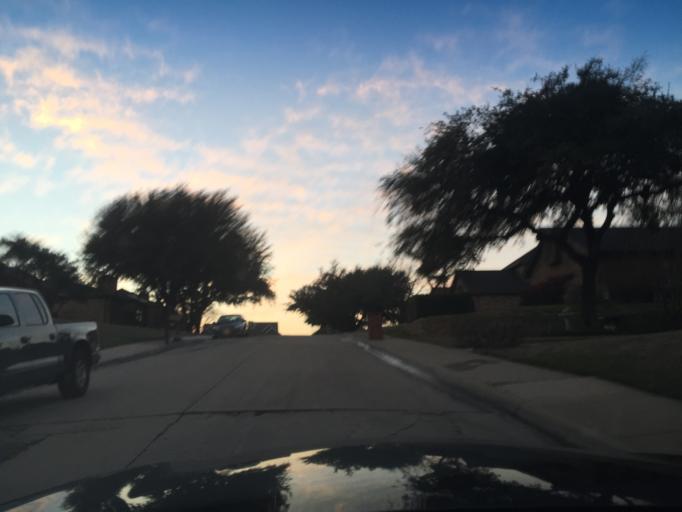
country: US
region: Texas
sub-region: Dallas County
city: Carrollton
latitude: 32.9887
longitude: -96.8934
